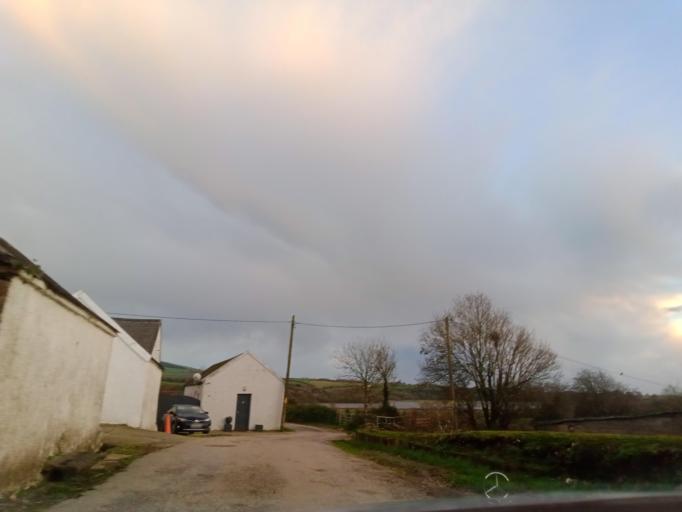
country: IE
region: Leinster
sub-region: Loch Garman
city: New Ross
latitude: 52.3359
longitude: -7.0076
